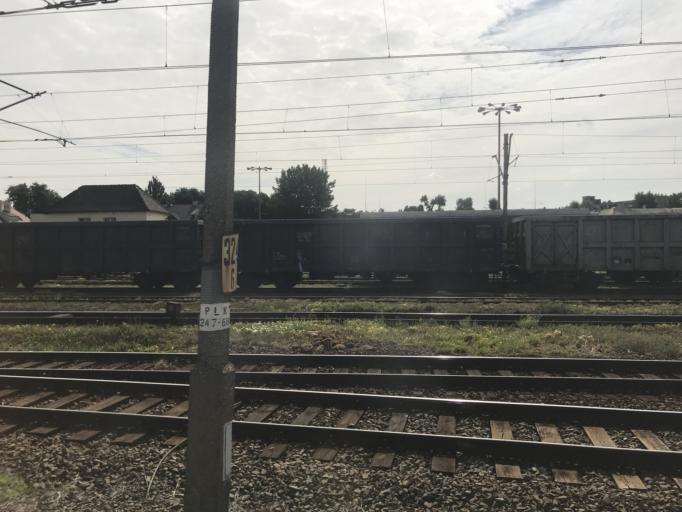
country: PL
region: Kujawsko-Pomorskie
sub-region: Powiat inowroclawski
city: Inowroclaw
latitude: 52.8028
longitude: 18.2417
